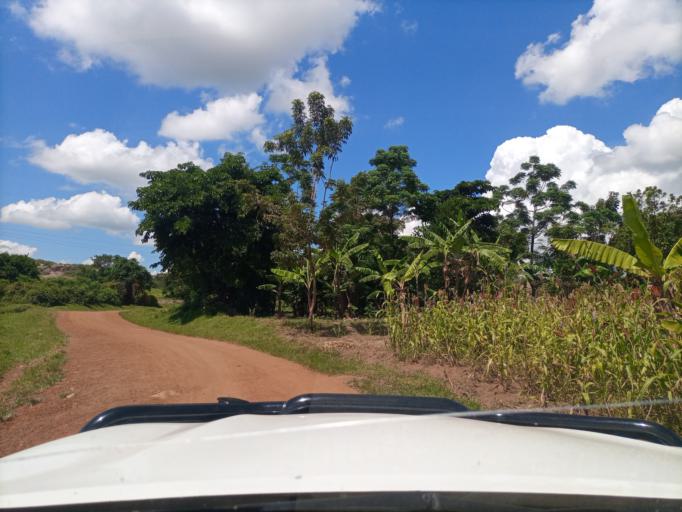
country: UG
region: Eastern Region
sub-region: Tororo District
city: Tororo
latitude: 0.6955
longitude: 34.0113
